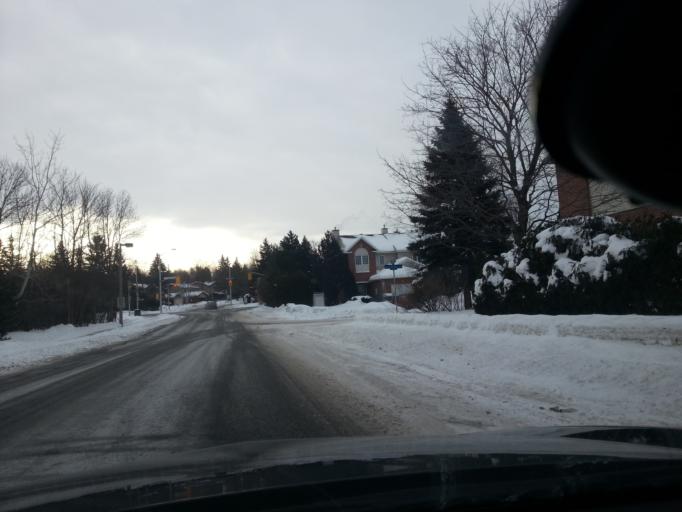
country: CA
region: Ontario
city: Bells Corners
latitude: 45.3116
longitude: -75.8968
